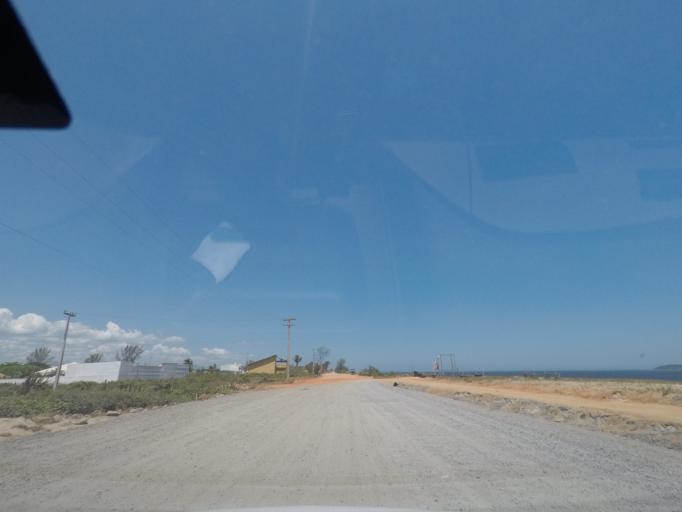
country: BR
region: Rio de Janeiro
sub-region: Marica
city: Marica
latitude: -22.9714
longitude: -42.9455
